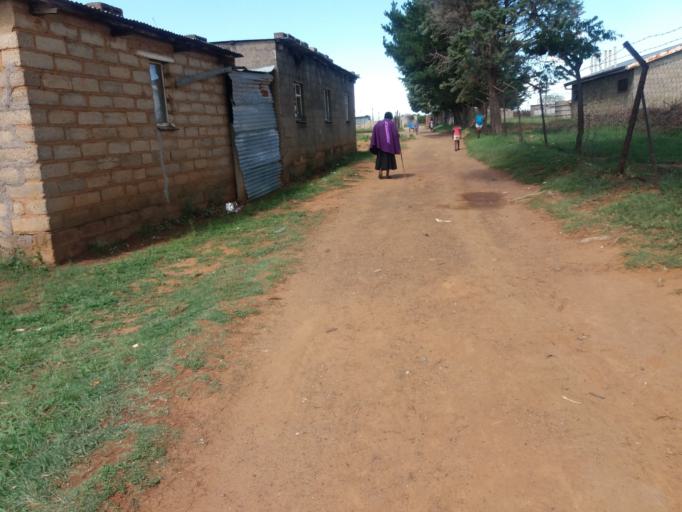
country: LS
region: Maseru
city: Maseru
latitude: -29.3707
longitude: 27.5086
